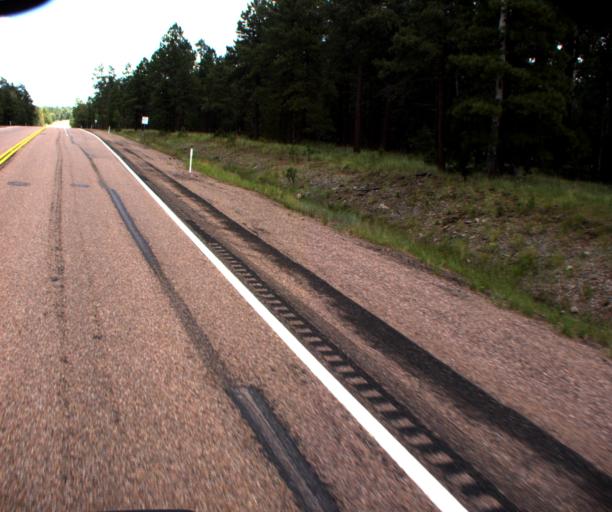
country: US
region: Arizona
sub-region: Apache County
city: Eagar
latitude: 34.0327
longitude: -109.6198
